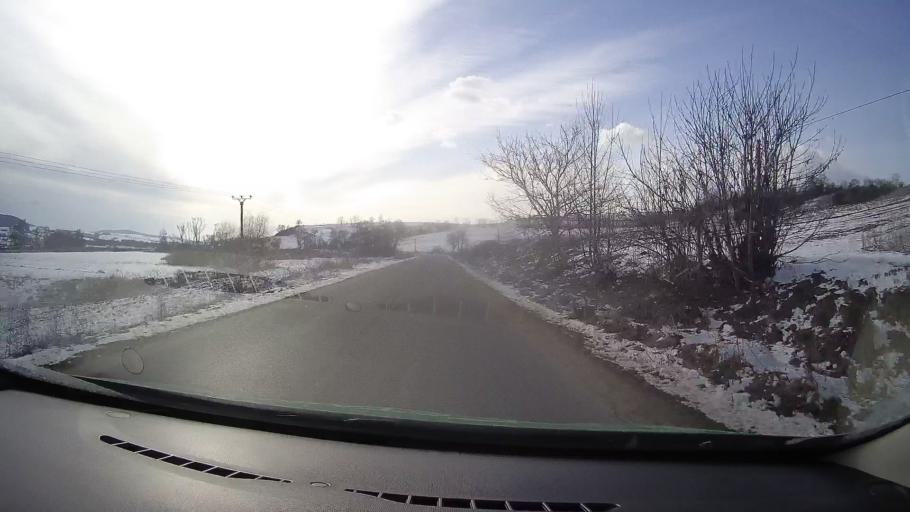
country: RO
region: Sibiu
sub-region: Comuna Iacobeni
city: Iacobeni
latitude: 46.0356
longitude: 24.7215
